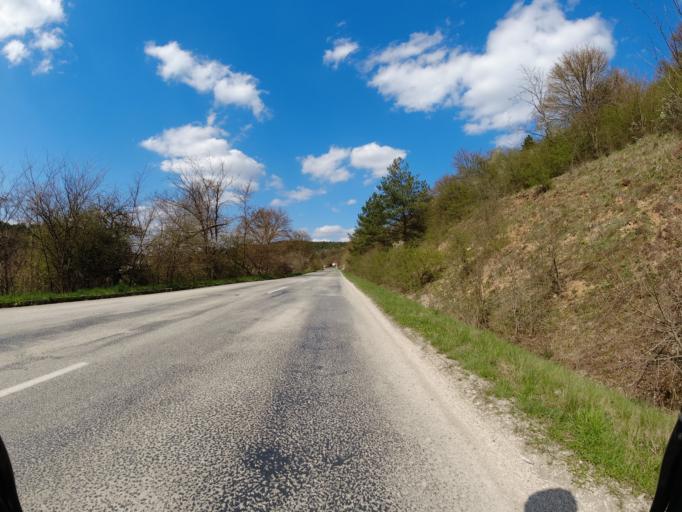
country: SK
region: Nitriansky
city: Stara Tura
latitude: 48.7473
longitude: 17.7227
